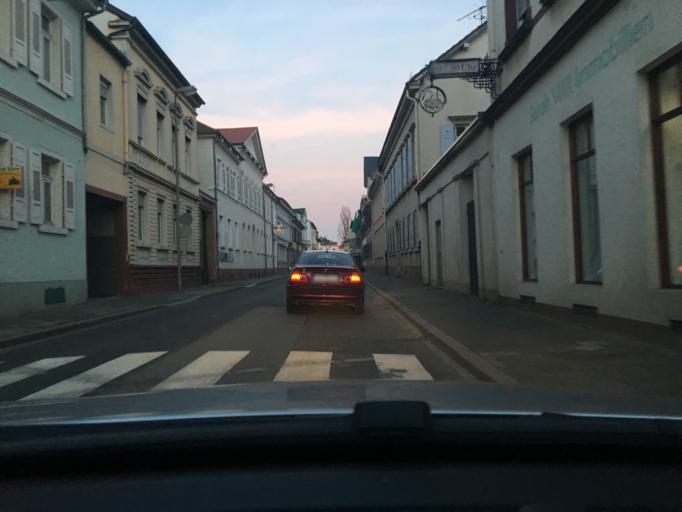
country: DE
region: Rheinland-Pfalz
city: Neustadt
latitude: 49.3556
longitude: 8.1386
